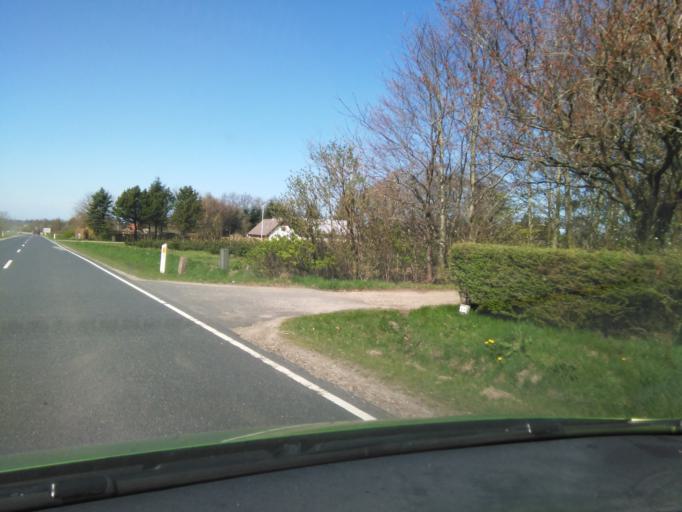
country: DK
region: South Denmark
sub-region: Billund Kommune
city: Grindsted
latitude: 55.6964
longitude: 8.9821
